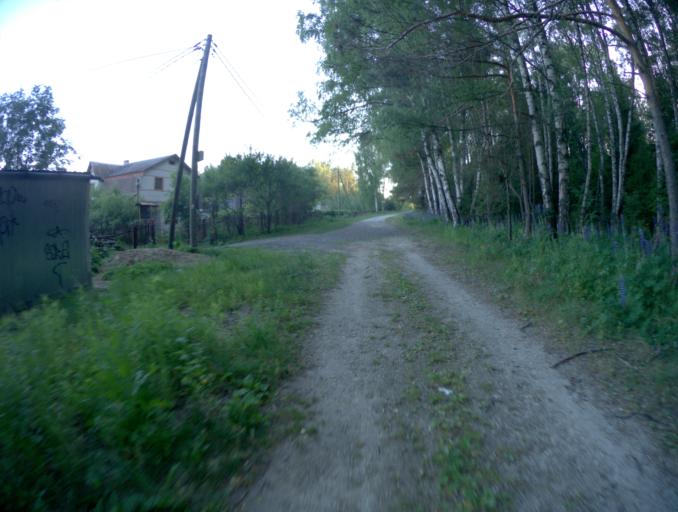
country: RU
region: Vladimir
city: Golovino
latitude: 55.9854
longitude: 40.5264
